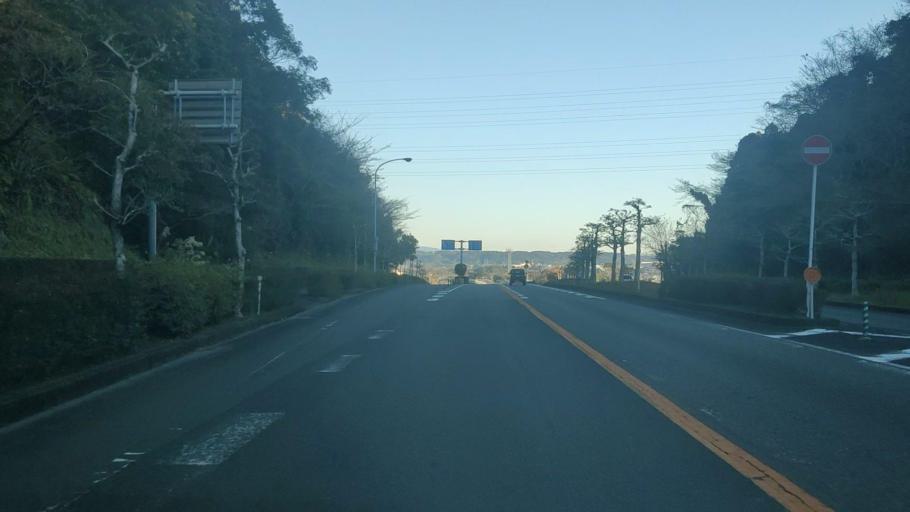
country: JP
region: Miyazaki
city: Tsuma
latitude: 32.0319
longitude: 131.4648
